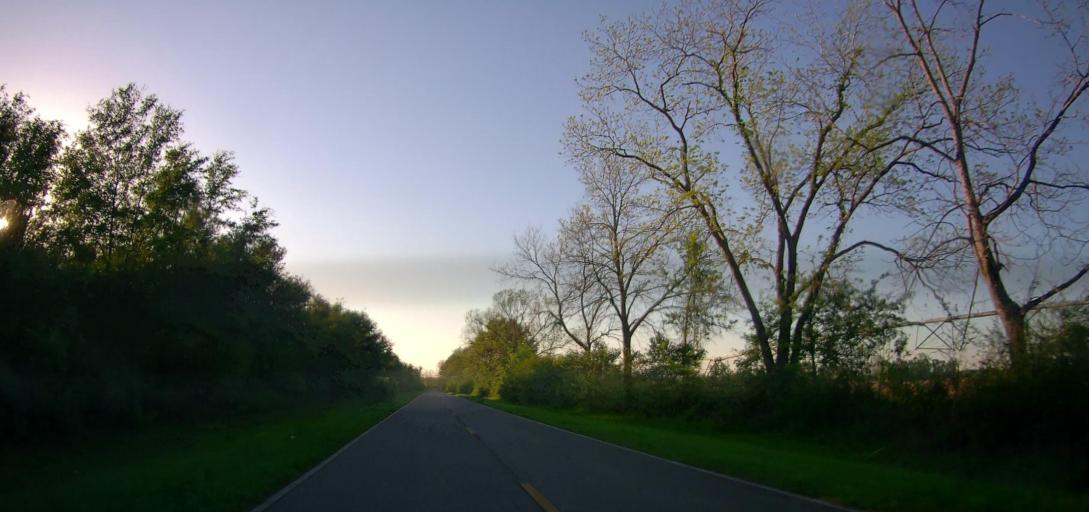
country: US
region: Georgia
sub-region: Ben Hill County
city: Fitzgerald
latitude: 31.6827
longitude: -83.2256
